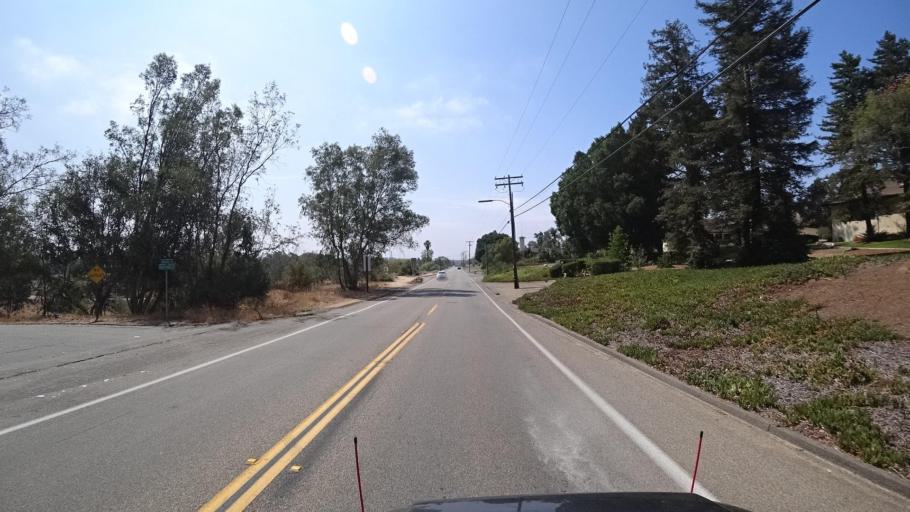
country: US
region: California
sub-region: San Diego County
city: Fallbrook
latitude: 33.3742
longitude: -117.2278
